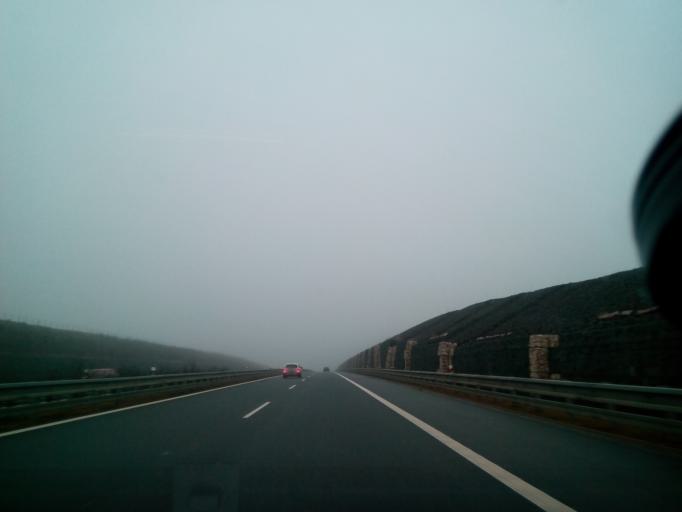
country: SK
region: Presovsky
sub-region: Okres Presov
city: Presov
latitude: 49.0066
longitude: 21.1449
